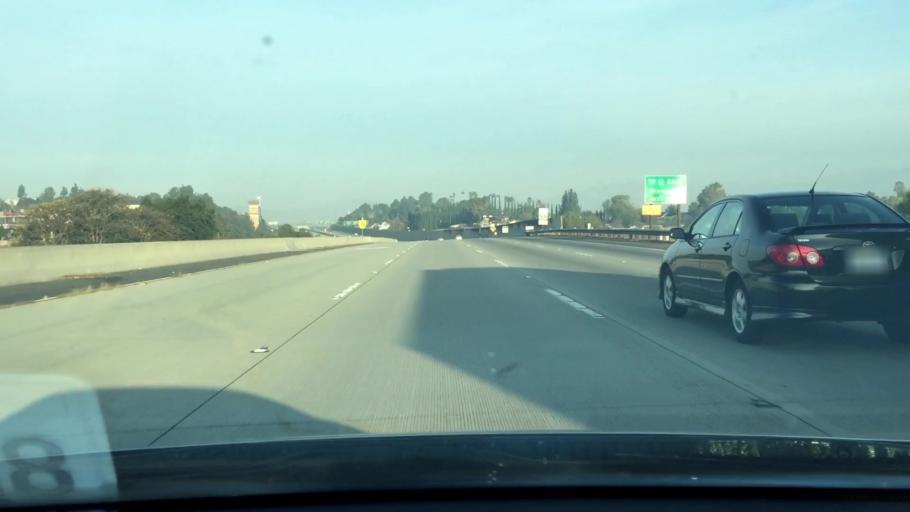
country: US
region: California
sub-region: San Bernardino County
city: Chino Hills
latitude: 34.0101
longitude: -117.7322
